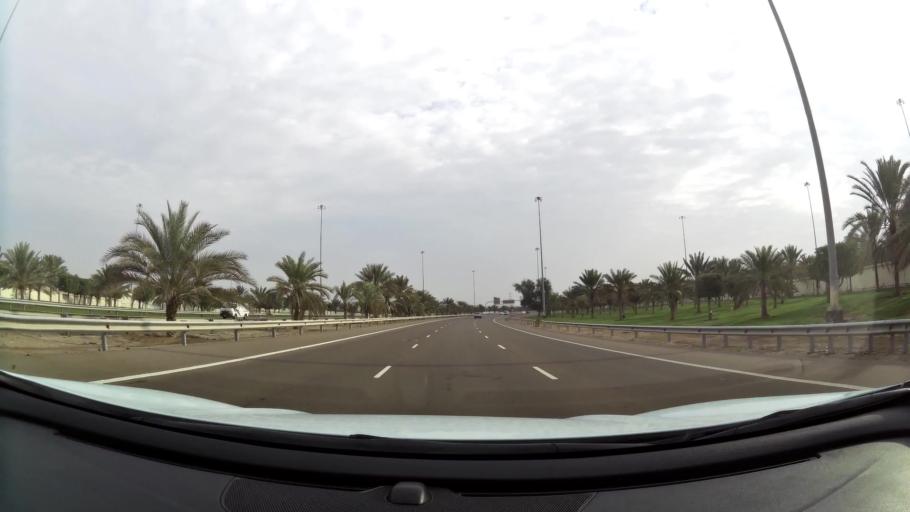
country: AE
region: Abu Dhabi
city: Al Ain
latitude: 24.1761
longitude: 55.1355
